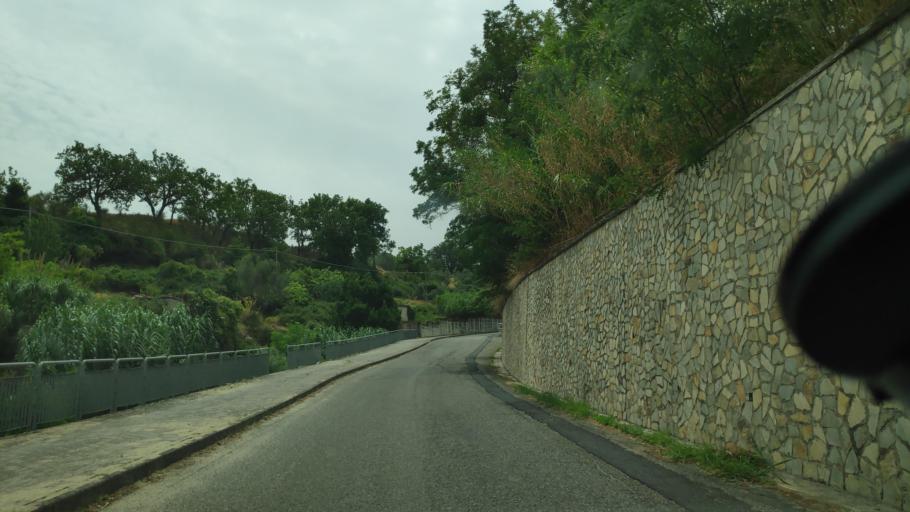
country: IT
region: Calabria
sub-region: Provincia di Catanzaro
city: Davoli
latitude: 38.6543
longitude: 16.4893
